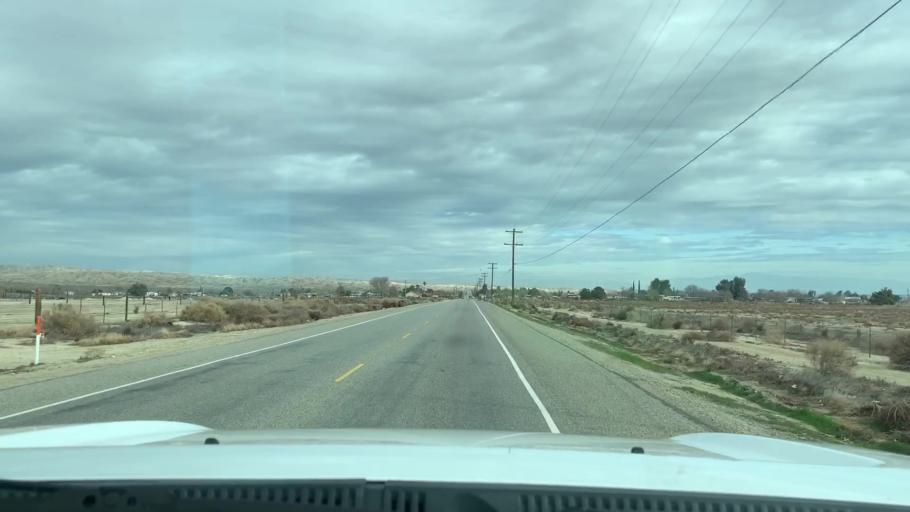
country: US
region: California
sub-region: Kern County
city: Ford City
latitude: 35.2143
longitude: -119.3982
